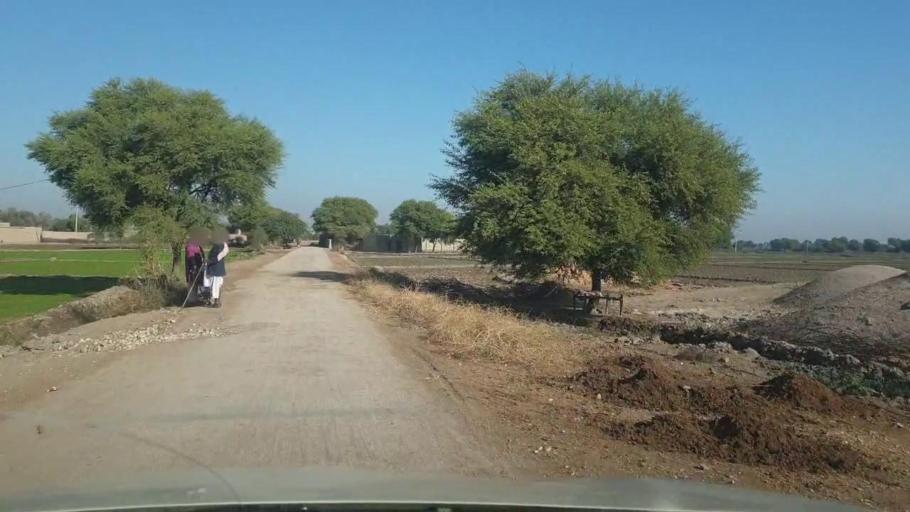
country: PK
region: Sindh
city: Bhan
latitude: 26.5599
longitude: 67.6640
